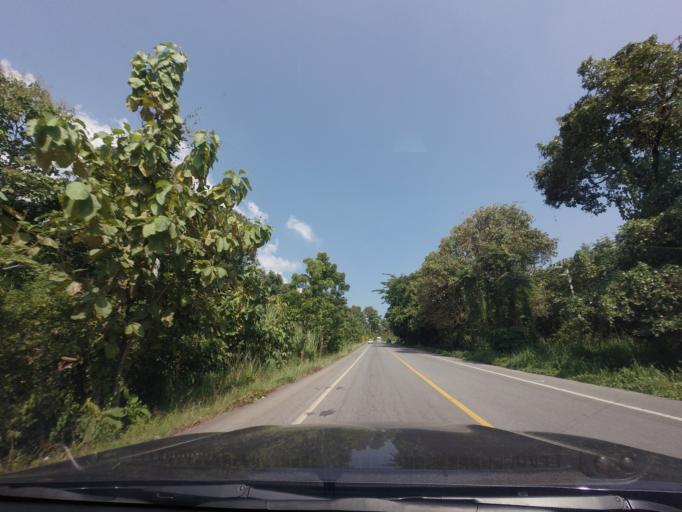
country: TH
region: Phitsanulok
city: Nakhon Thai
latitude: 17.1285
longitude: 100.7385
